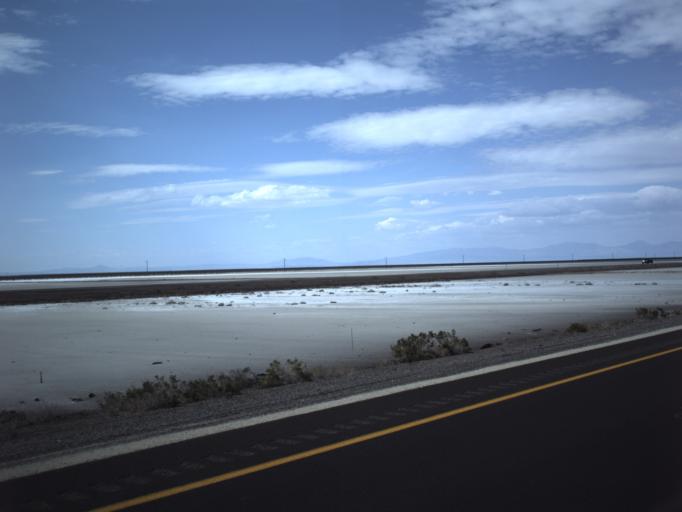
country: US
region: Utah
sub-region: Tooele County
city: Wendover
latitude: 40.7326
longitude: -113.5344
